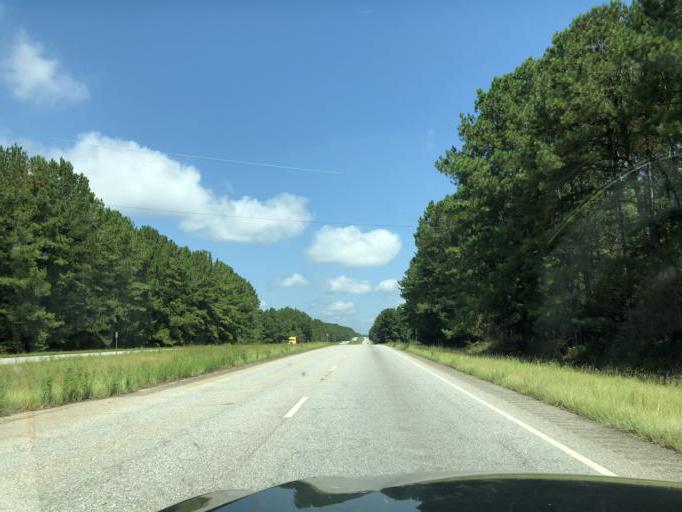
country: US
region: Alabama
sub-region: Henry County
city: Abbeville
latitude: 31.6546
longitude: -85.2802
